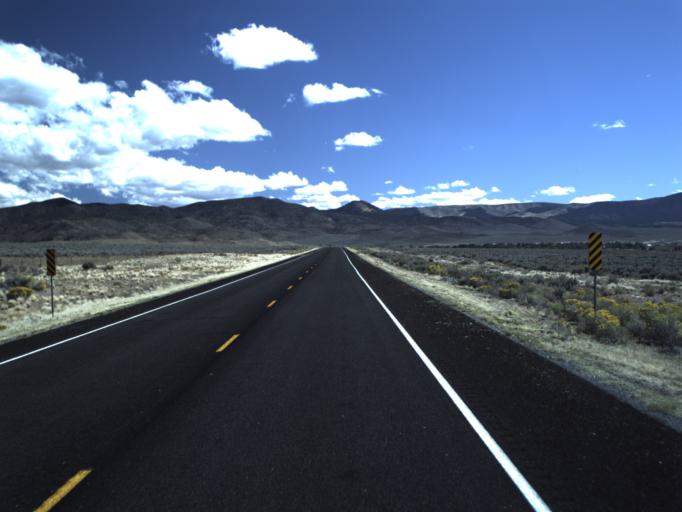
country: US
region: Utah
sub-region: Beaver County
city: Milford
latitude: 38.2446
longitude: -112.9416
